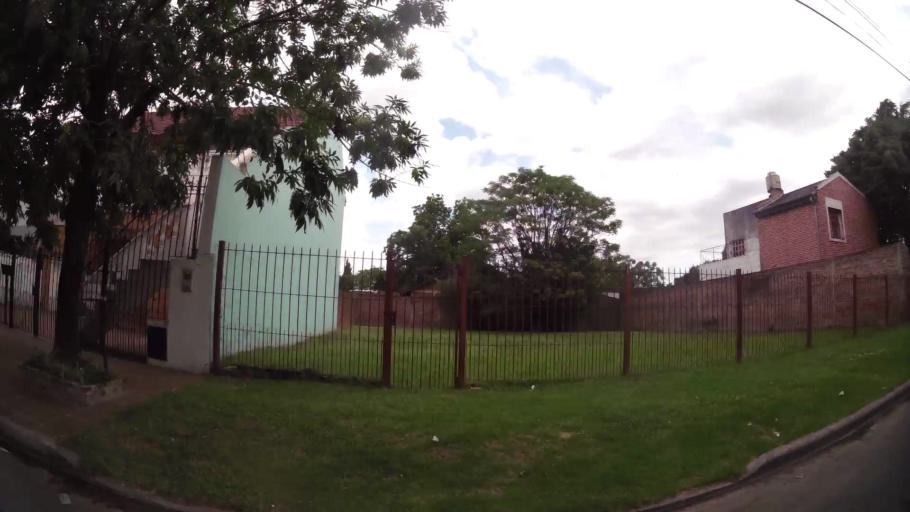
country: AR
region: Buenos Aires
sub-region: Partido de Tigre
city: Tigre
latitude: -34.4655
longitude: -58.6495
